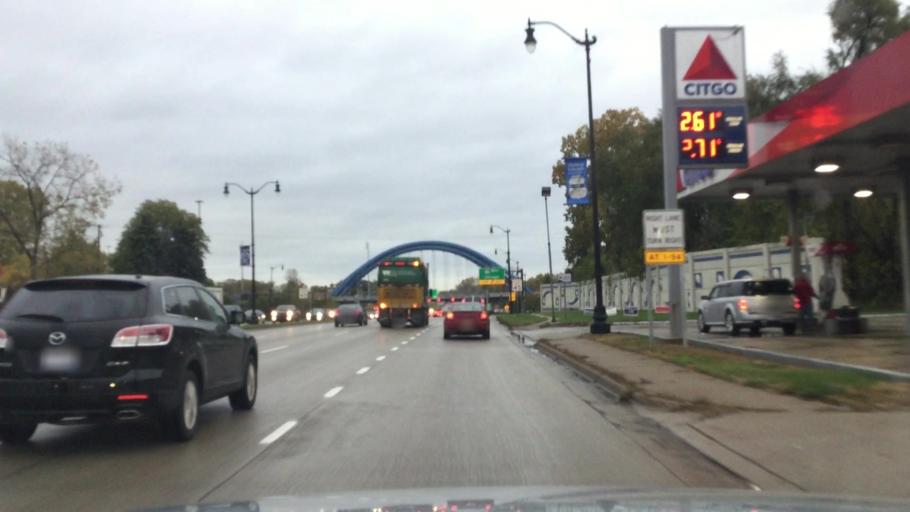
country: US
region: Michigan
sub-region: Wayne County
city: Taylor
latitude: 42.2683
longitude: -83.2706
